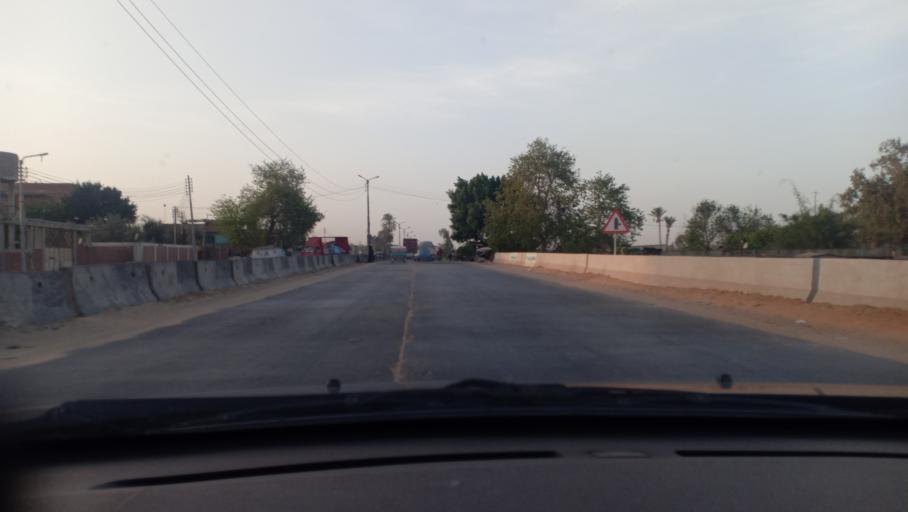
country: EG
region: Muhafazat al Gharbiyah
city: Zifta
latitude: 30.6563
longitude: 31.2840
